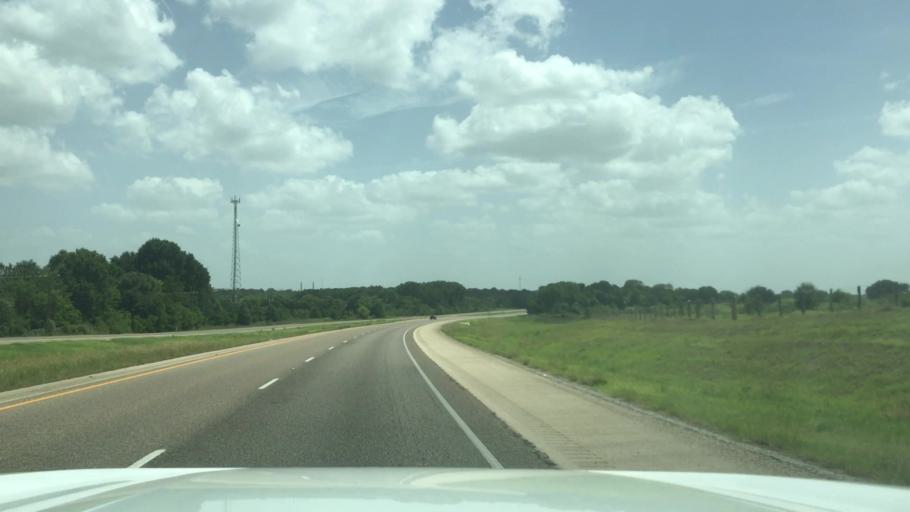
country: US
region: Texas
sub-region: Robertson County
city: Calvert
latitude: 31.1238
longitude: -96.7134
